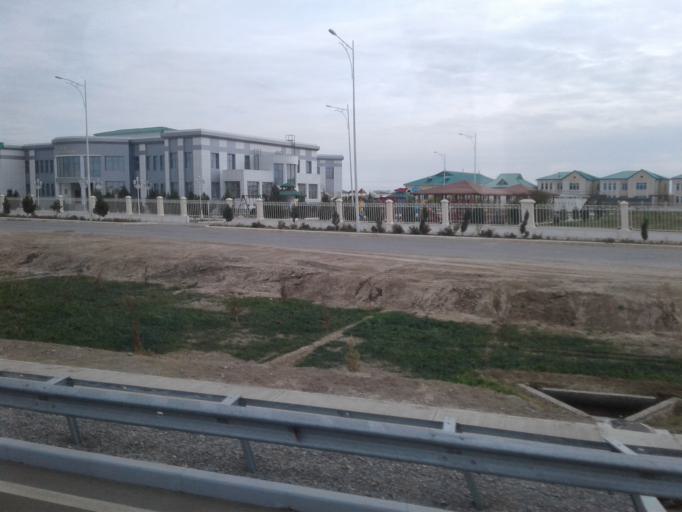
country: TM
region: Lebap
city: Turkmenabat
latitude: 38.9870
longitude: 63.5620
